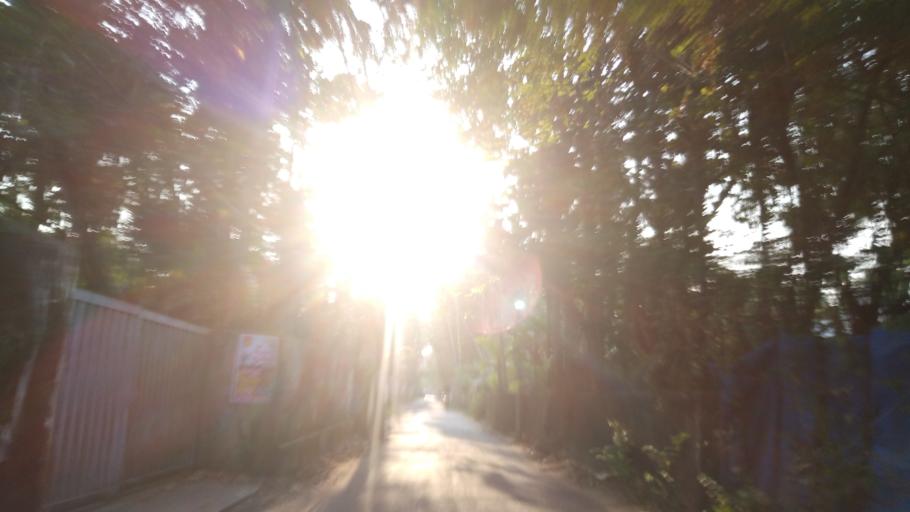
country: IN
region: Kerala
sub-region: Thrissur District
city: Kodungallur
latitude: 10.1349
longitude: 76.1947
